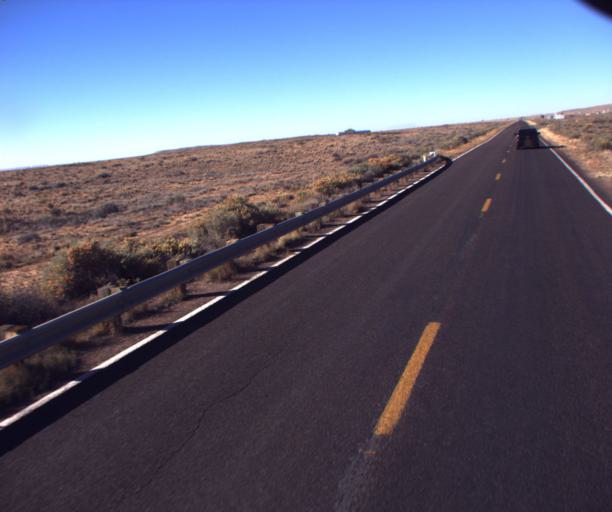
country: US
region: Arizona
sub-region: Navajo County
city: First Mesa
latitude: 35.8029
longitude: -110.4342
